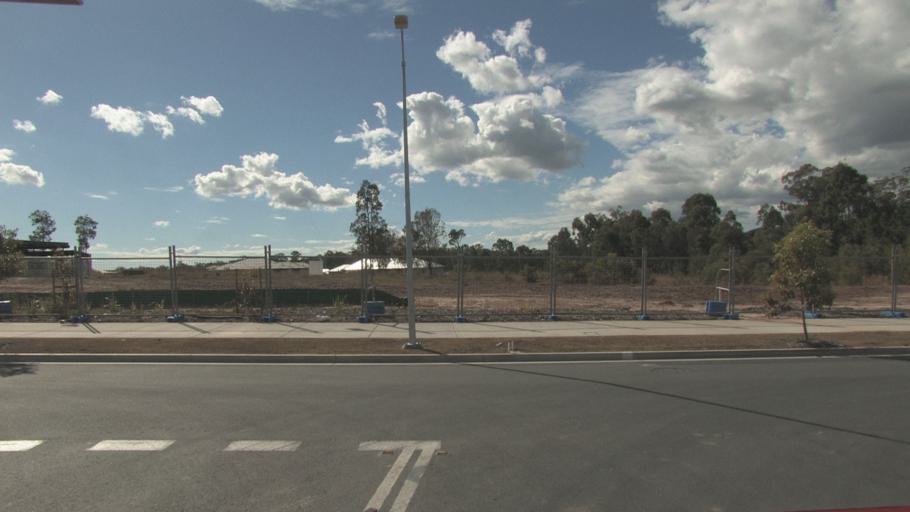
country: AU
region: Queensland
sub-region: Logan
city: Chambers Flat
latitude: -27.8035
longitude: 153.1198
